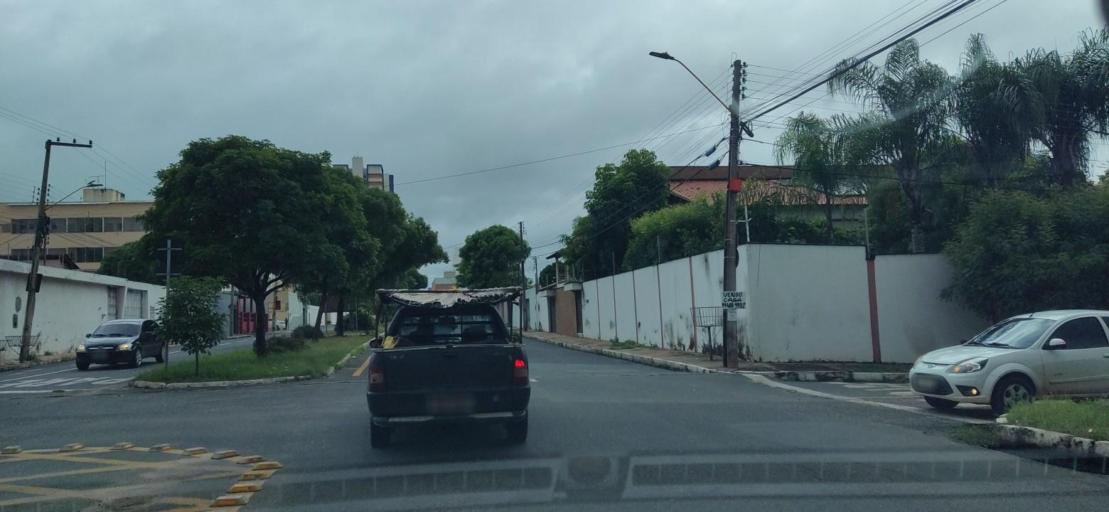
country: BR
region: Piaui
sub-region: Teresina
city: Teresina
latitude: -5.0704
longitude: -42.7515
